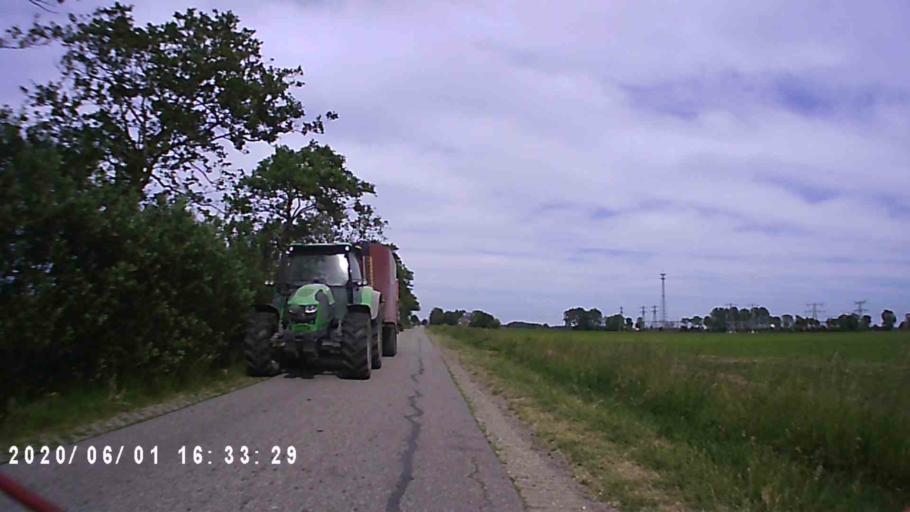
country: NL
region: Friesland
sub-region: Gemeente Leeuwarden
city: Camminghaburen
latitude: 53.1919
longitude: 5.8668
